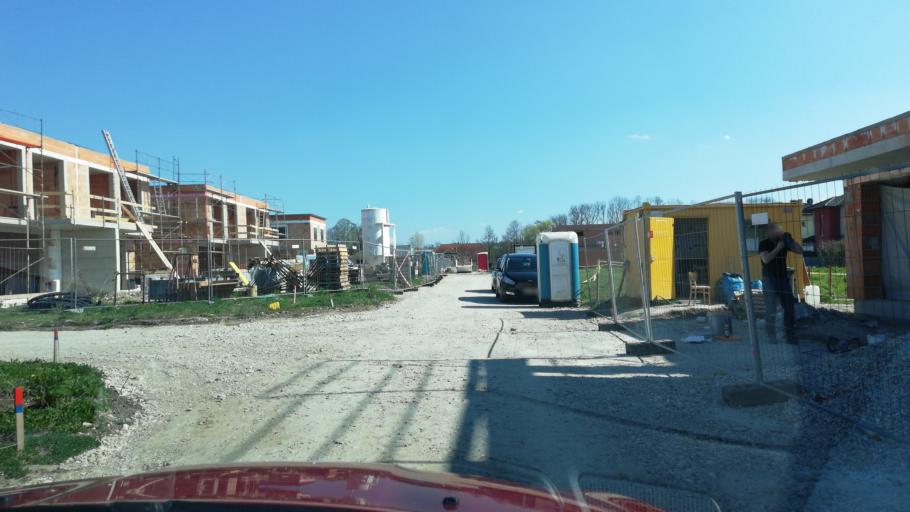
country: AT
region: Upper Austria
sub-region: Politischer Bezirk Linz-Land
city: Horsching
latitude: 48.2080
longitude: 14.1963
